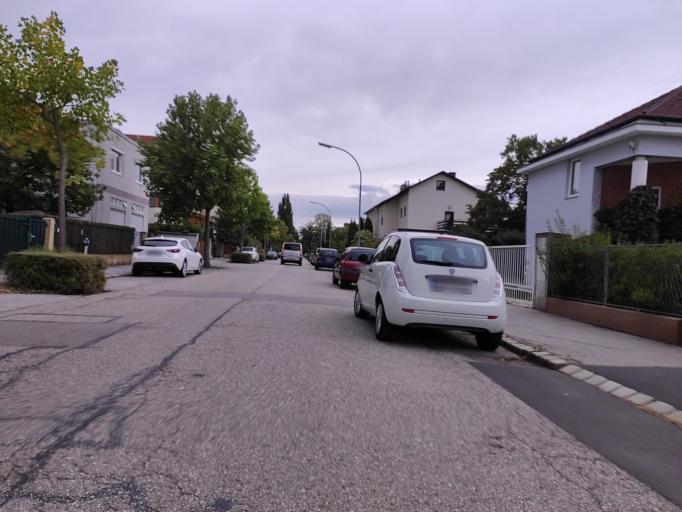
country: AT
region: Lower Austria
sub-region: Politischer Bezirk Baden
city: Baden
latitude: 48.0022
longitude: 16.2369
